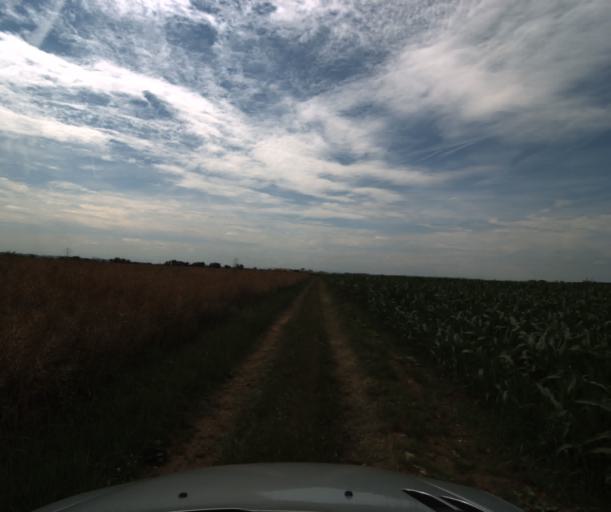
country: FR
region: Midi-Pyrenees
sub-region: Departement de la Haute-Garonne
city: Lacasse
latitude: 43.4181
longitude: 1.2631
